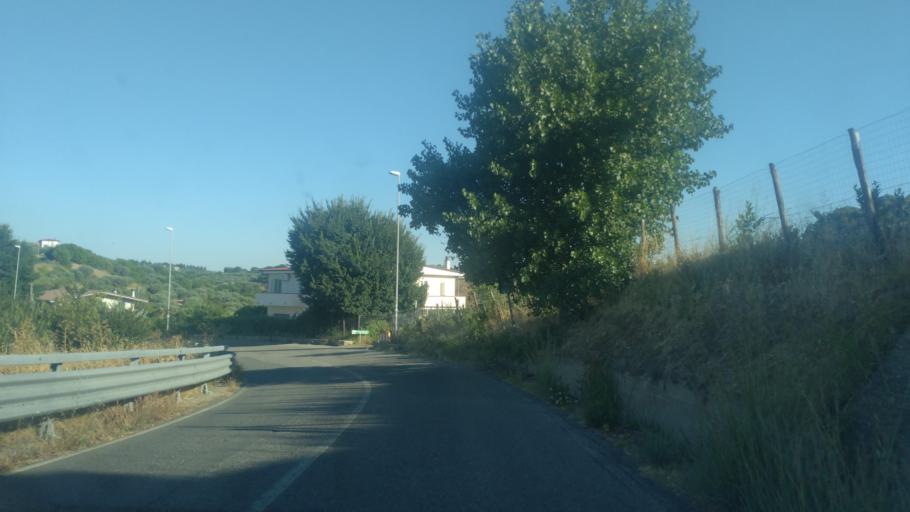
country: IT
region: Calabria
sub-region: Provincia di Catanzaro
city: Staletti
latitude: 38.7661
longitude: 16.5322
